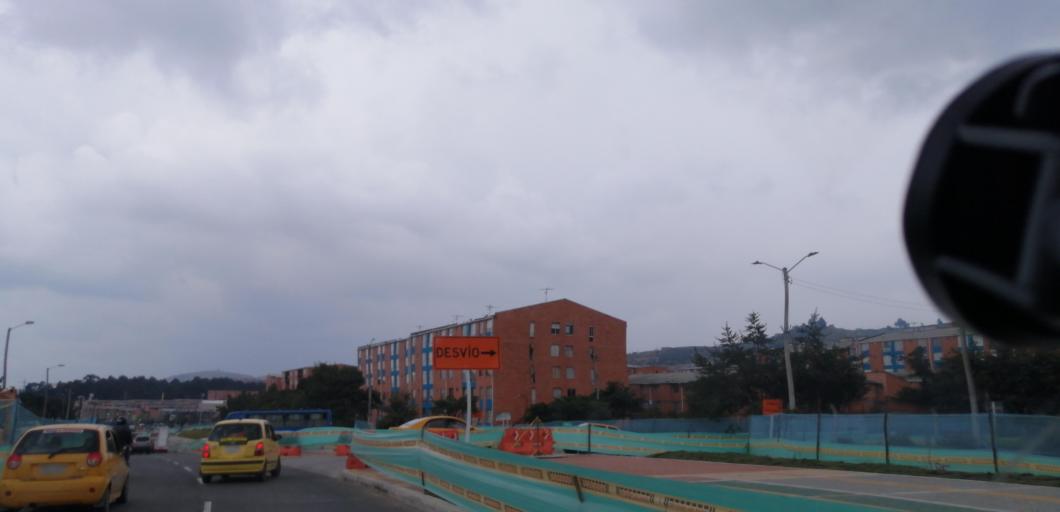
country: CO
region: Bogota D.C.
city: Bogota
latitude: 4.5283
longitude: -74.1190
